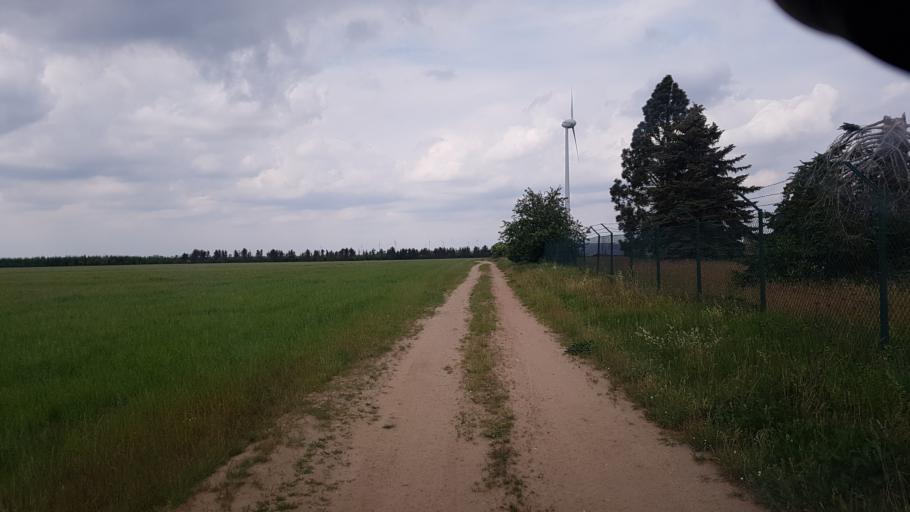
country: DE
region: Brandenburg
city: Dahme
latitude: 51.8777
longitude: 13.4110
